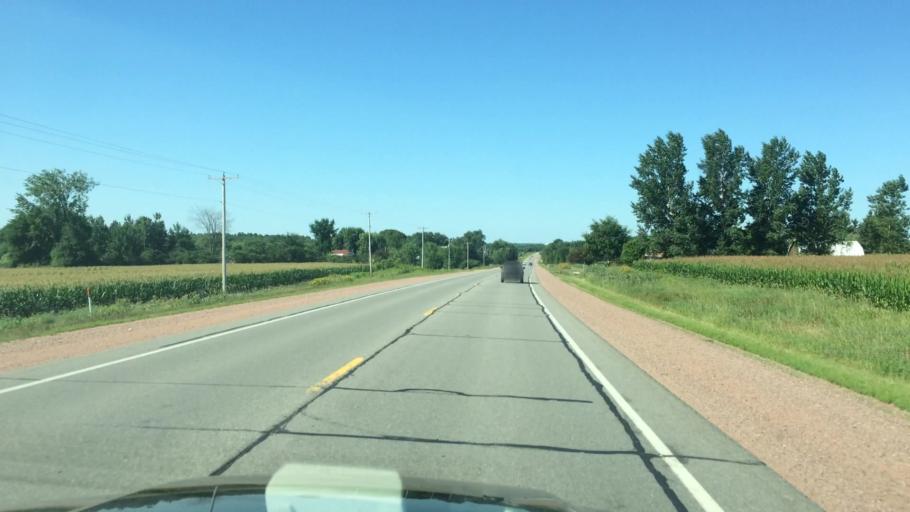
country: US
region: Wisconsin
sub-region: Marathon County
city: Stratford
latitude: 44.7263
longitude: -90.0922
